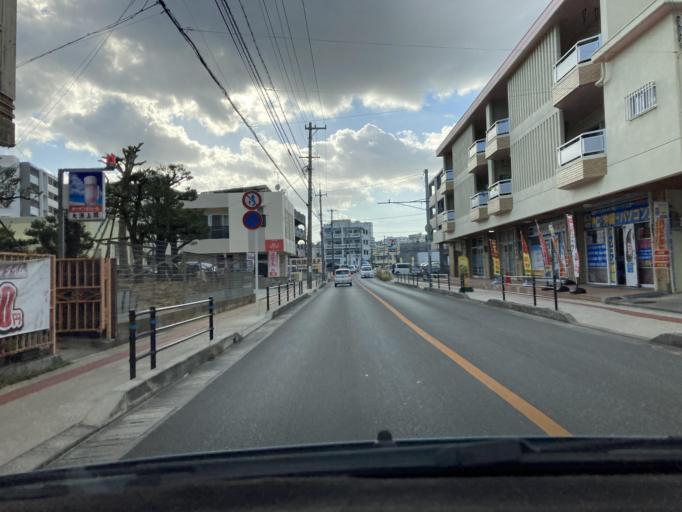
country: JP
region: Okinawa
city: Okinawa
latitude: 26.3338
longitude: 127.8153
